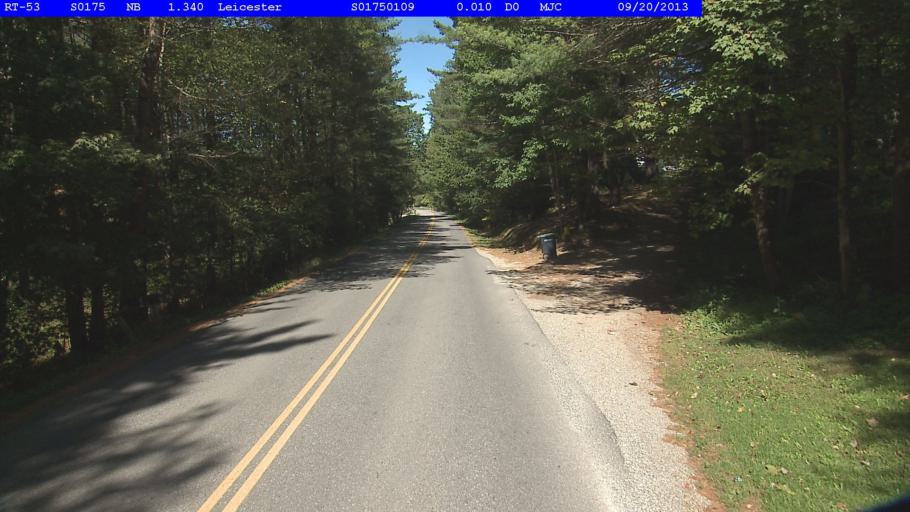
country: US
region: Vermont
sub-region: Rutland County
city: Brandon
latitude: 43.8461
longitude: -73.0572
